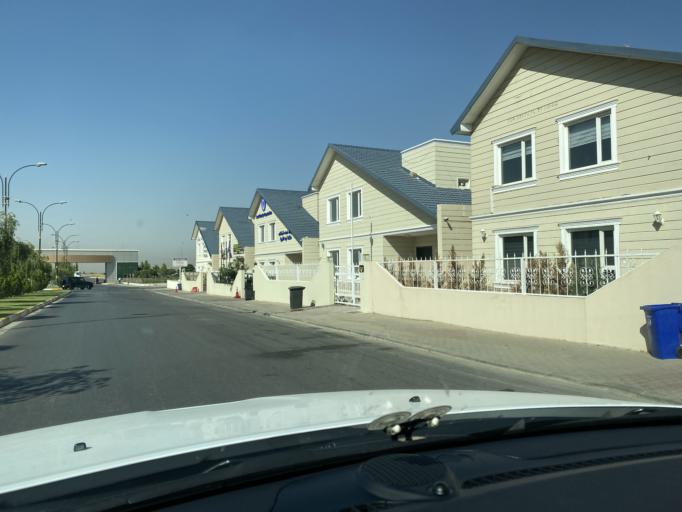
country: IQ
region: Arbil
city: Erbil
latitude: 36.2402
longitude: 44.0499
